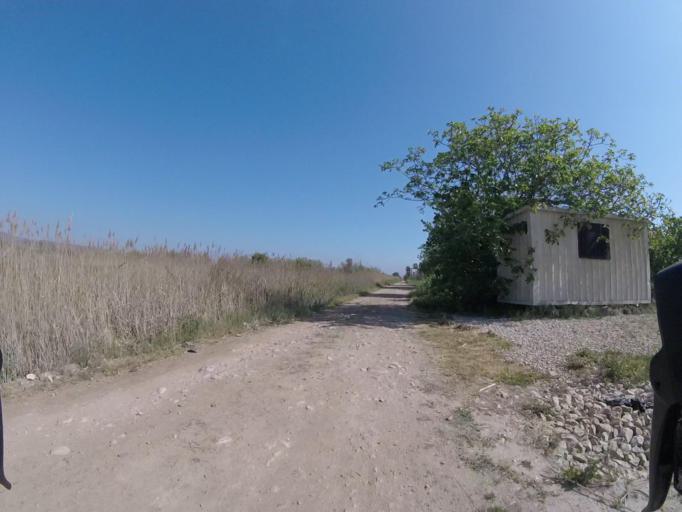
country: ES
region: Valencia
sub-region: Provincia de Castello
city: Orpesa/Oropesa del Mar
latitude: 40.1517
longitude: 0.1680
